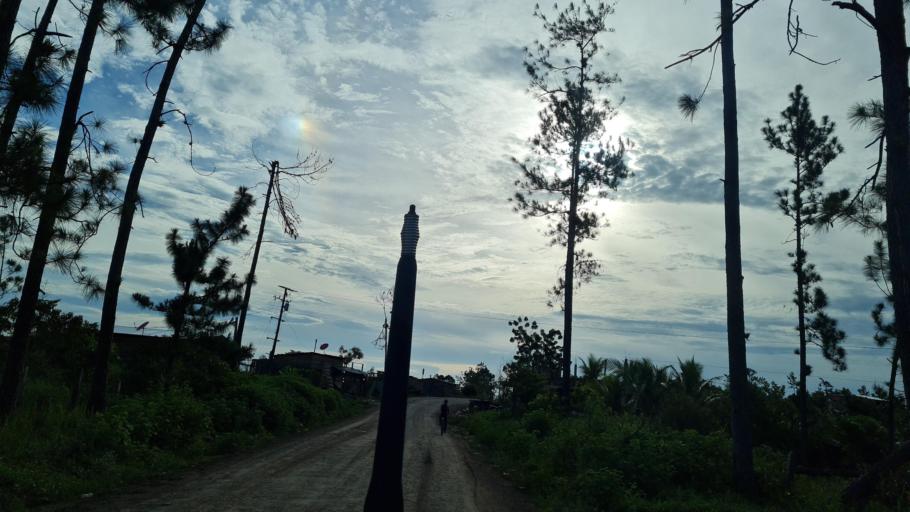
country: NI
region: Atlantico Sur
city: La Cruz de Rio Grande
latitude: 13.5643
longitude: -84.3128
